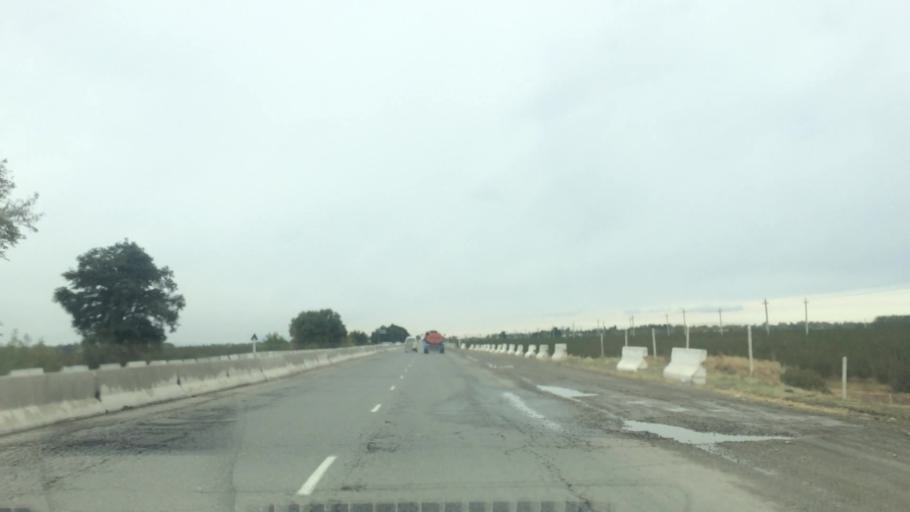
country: UZ
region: Samarqand
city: Bulung'ur
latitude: 39.7541
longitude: 67.2345
